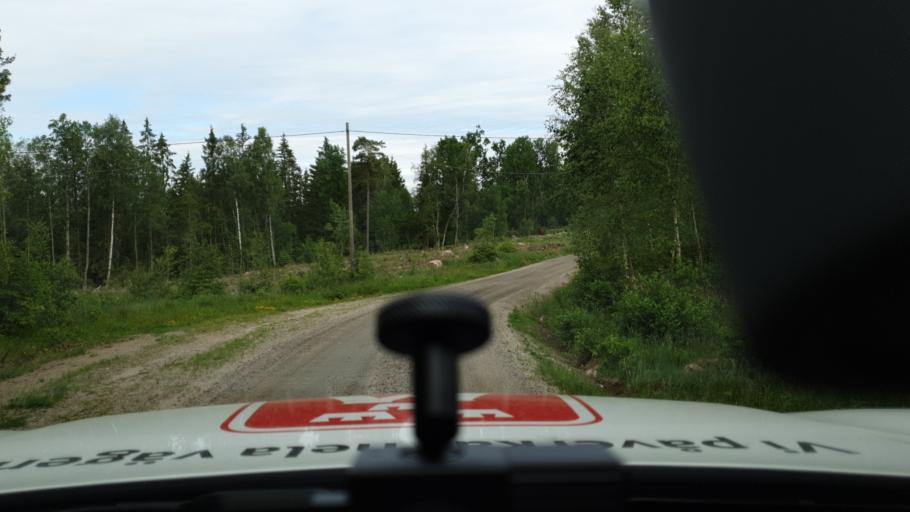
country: SE
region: Vaestra Goetaland
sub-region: Falkopings Kommun
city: Falkoeping
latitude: 58.0280
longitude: 13.6690
